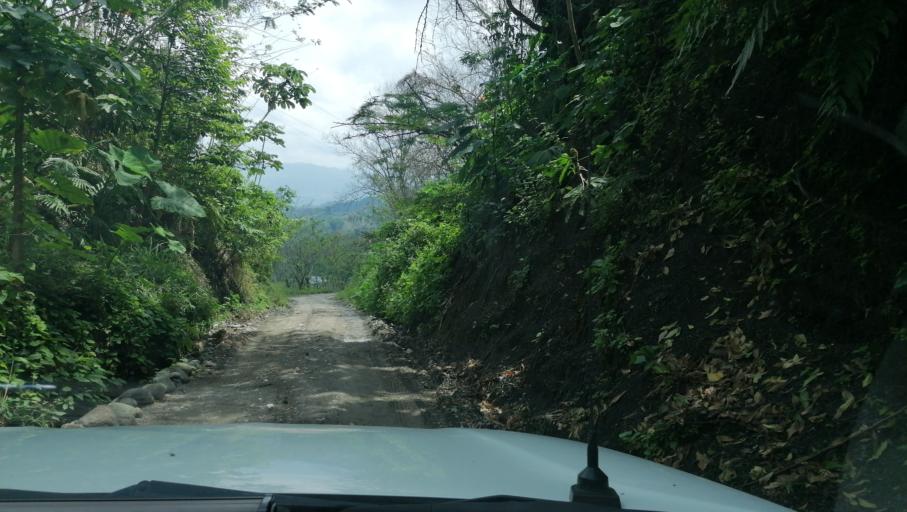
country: MX
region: Chiapas
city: Ixtacomitan
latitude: 17.4441
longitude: -93.1997
